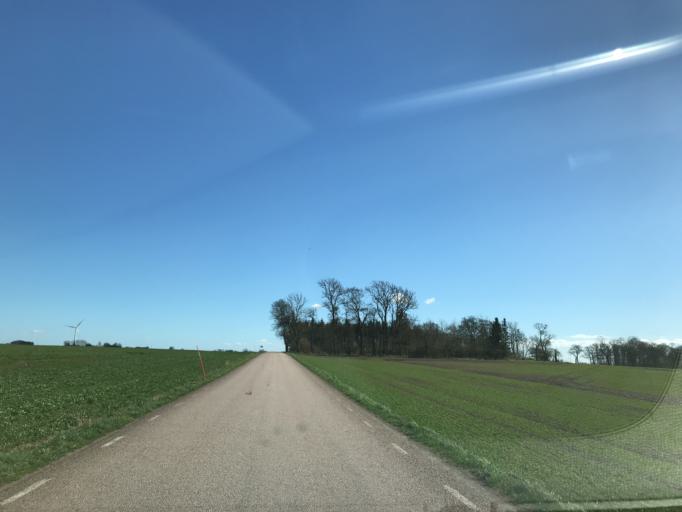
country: SE
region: Skane
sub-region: Landskrona
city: Asmundtorp
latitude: 55.9127
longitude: 13.0034
